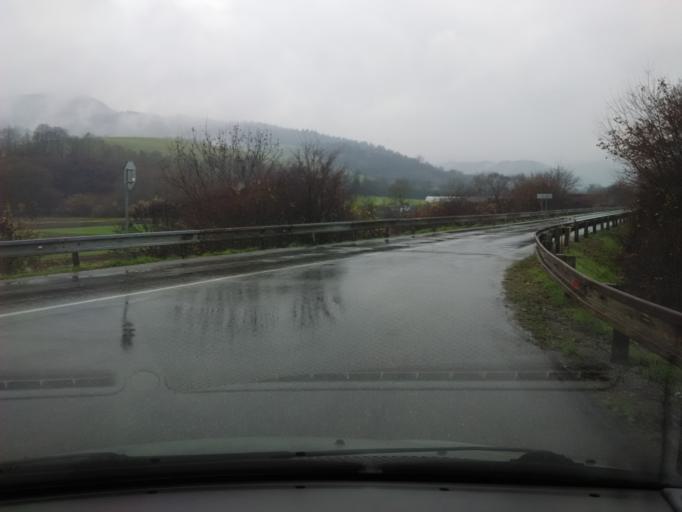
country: SK
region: Trenciansky
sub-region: Okres Povazska Bystrica
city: Povazska Bystrica
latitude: 49.1650
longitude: 18.4696
